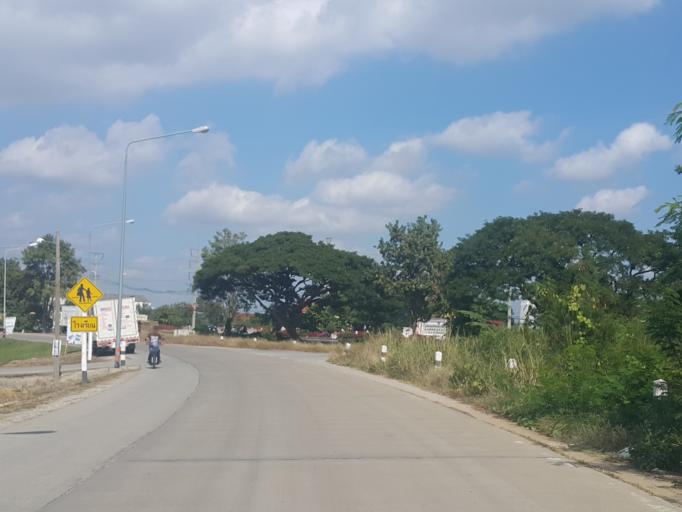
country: TH
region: Chiang Mai
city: Saraphi
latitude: 18.7373
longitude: 99.0360
